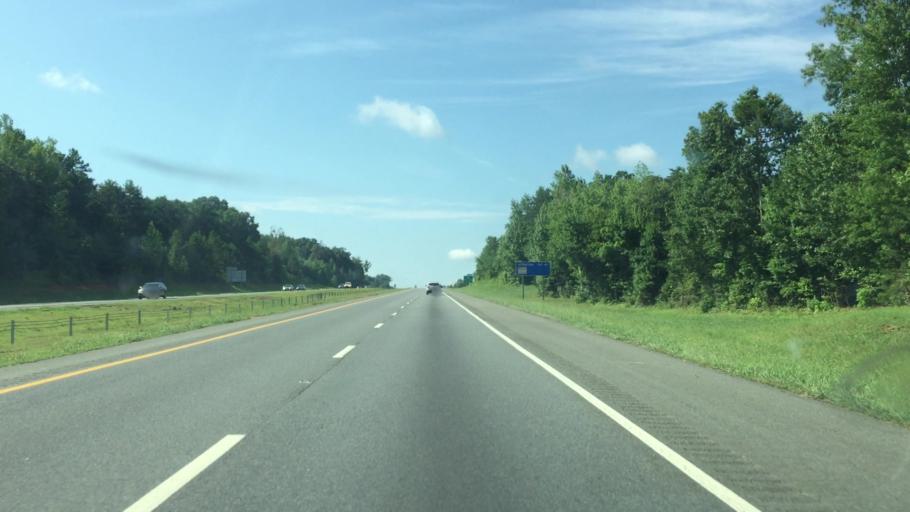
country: US
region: North Carolina
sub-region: Mecklenburg County
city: Mint Hill
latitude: 35.1937
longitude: -80.6294
